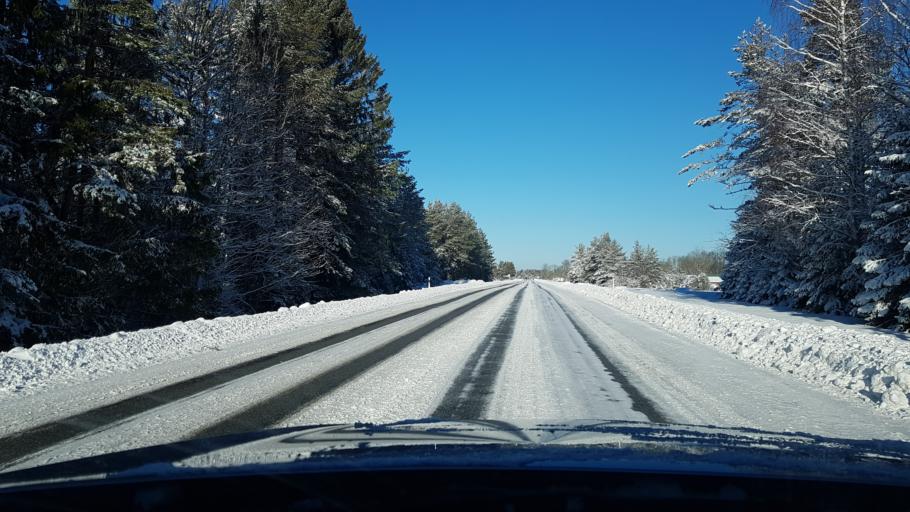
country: EE
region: Hiiumaa
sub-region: Kaerdla linn
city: Kardla
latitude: 58.9503
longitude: 22.7720
